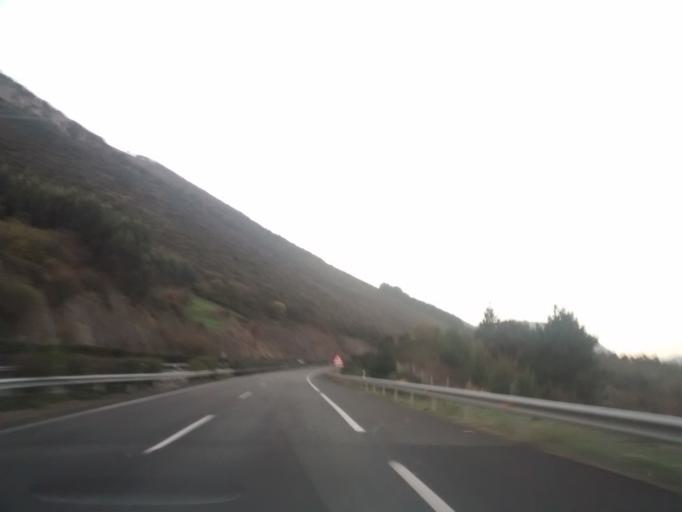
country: ES
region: Cantabria
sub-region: Provincia de Cantabria
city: Castro-Urdiales
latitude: 43.3982
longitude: -3.2693
